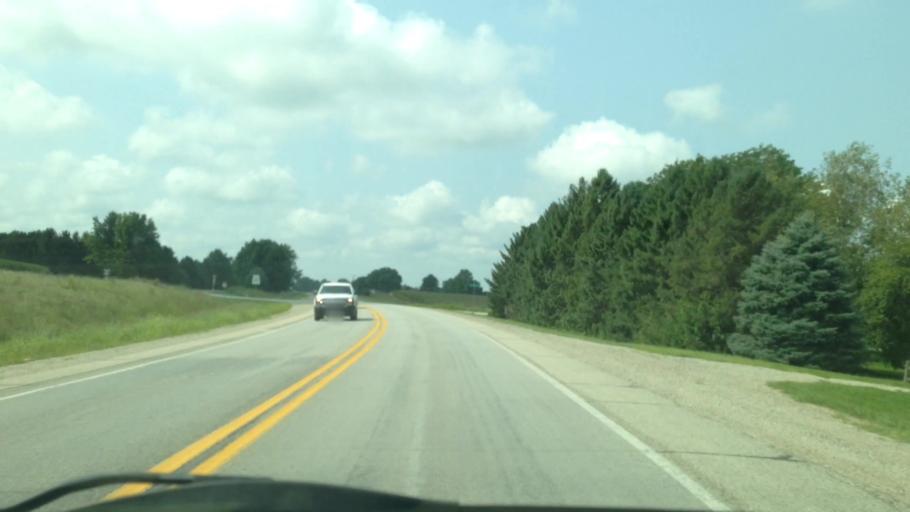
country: US
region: Iowa
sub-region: Linn County
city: Fairfax
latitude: 41.9105
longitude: -91.7923
